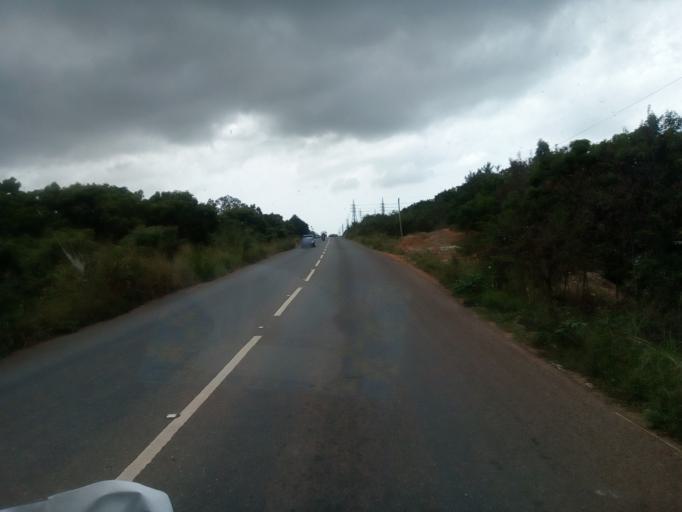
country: GH
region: Greater Accra
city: Dome
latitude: 5.6447
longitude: -0.2043
